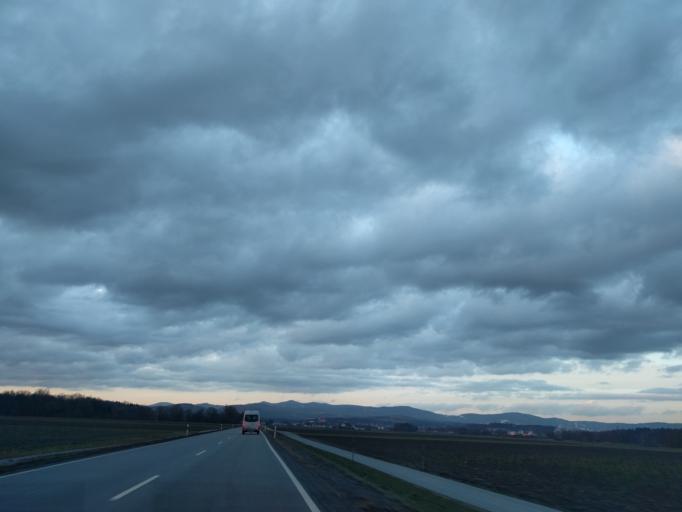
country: DE
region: Bavaria
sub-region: Lower Bavaria
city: Winzer
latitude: 48.7431
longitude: 13.0589
